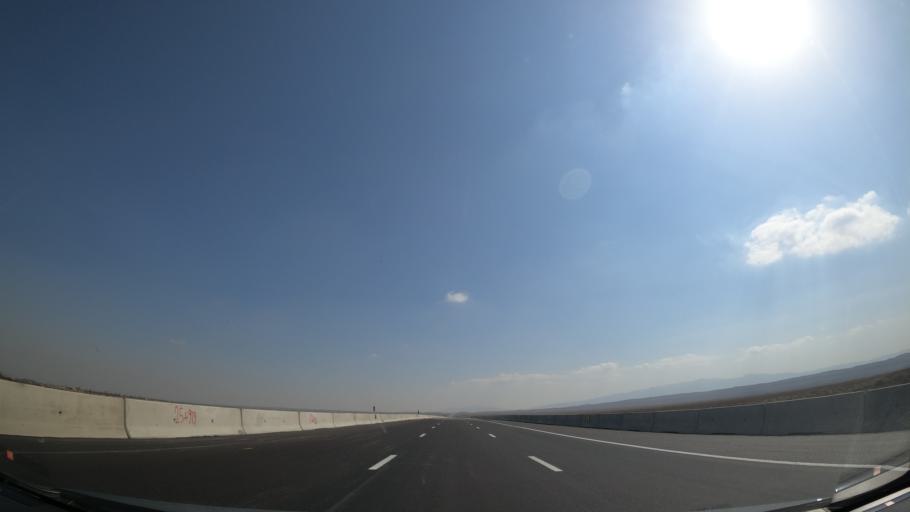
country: IR
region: Alborz
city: Nazarabad
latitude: 35.8370
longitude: 50.4918
